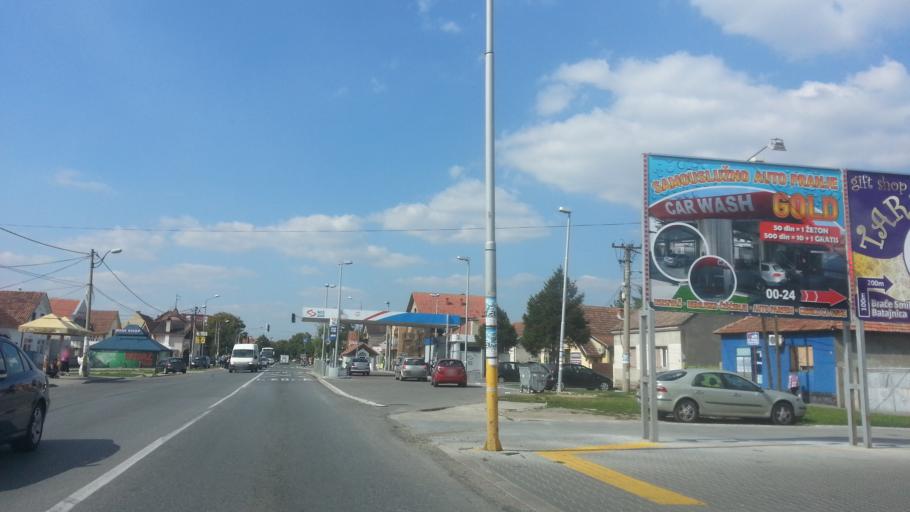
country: RS
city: Novi Banovci
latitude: 44.8991
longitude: 20.2876
